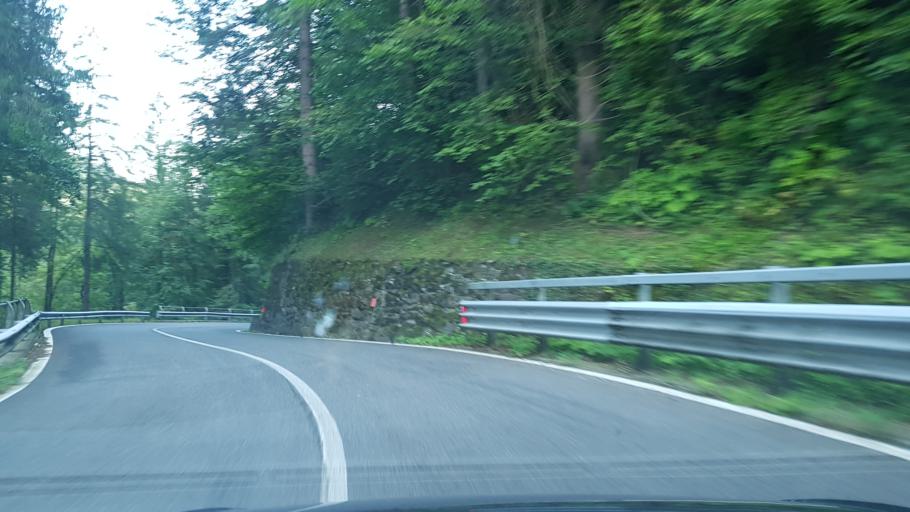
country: IT
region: Friuli Venezia Giulia
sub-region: Provincia di Udine
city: Comeglians
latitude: 46.5268
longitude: 12.8693
